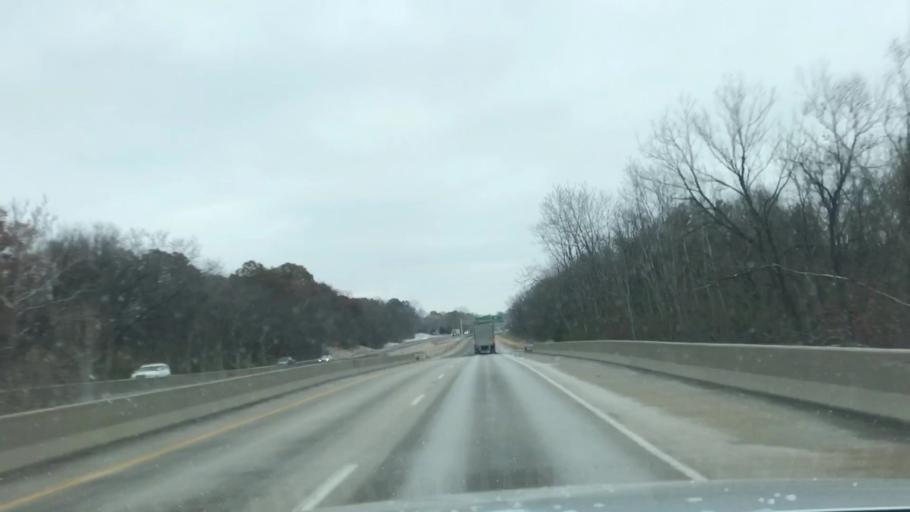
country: US
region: Illinois
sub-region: Madison County
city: Glen Carbon
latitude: 38.7568
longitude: -89.9668
